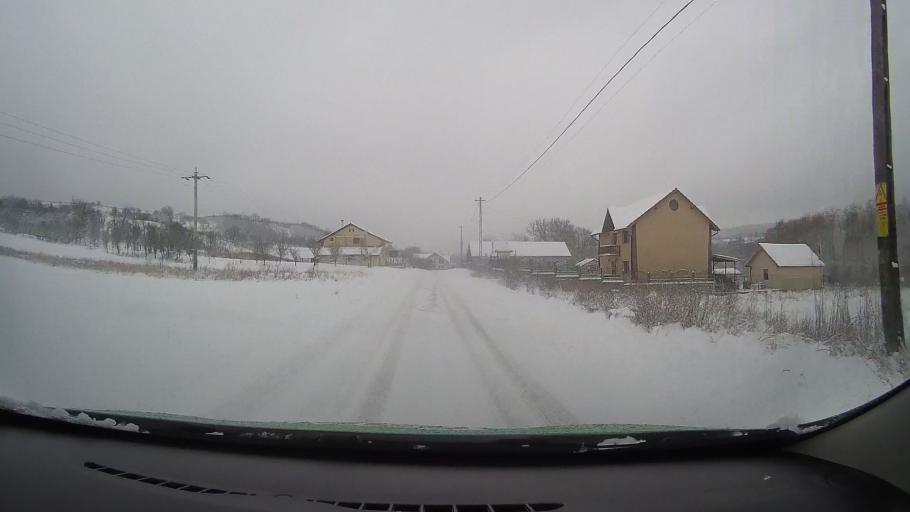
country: RO
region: Hunedoara
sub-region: Comuna Carjiti
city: Carjiti
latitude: 45.8301
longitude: 22.8446
